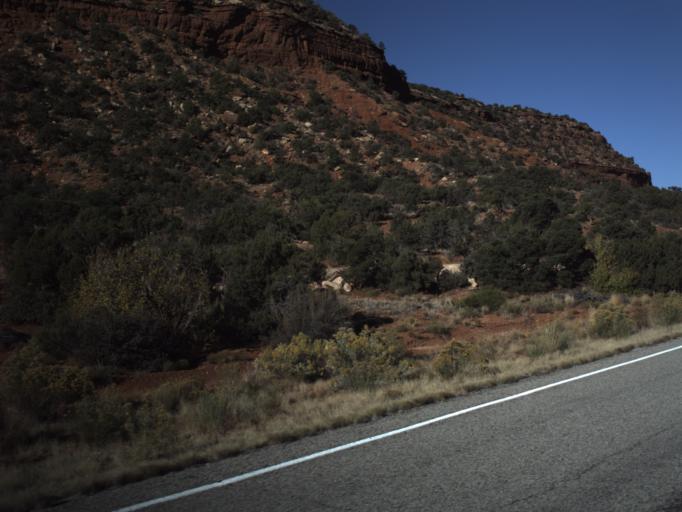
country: US
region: Utah
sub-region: San Juan County
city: Blanding
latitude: 37.6006
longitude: -110.0569
